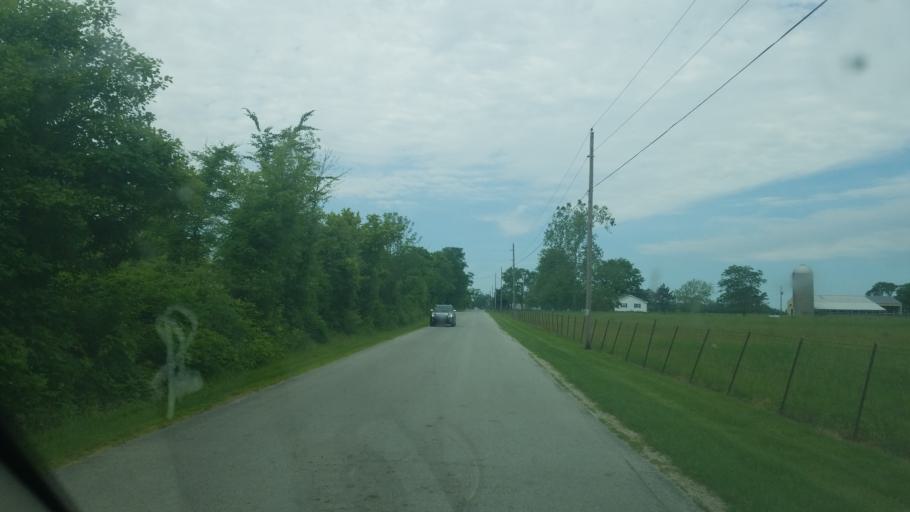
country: US
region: Ohio
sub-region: Wood County
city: North Baltimore
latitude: 41.2220
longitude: -83.6345
